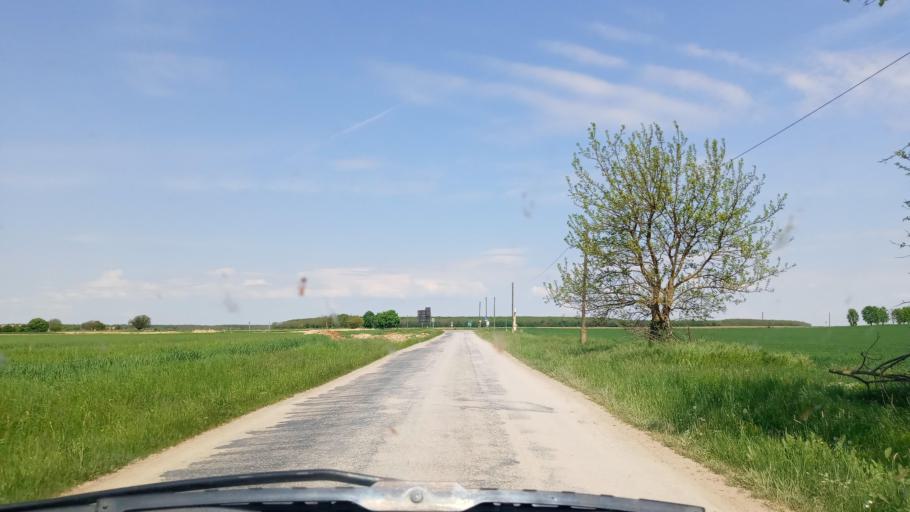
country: HR
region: Osjecko-Baranjska
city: Beli Manastir
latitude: 45.8728
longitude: 18.5823
